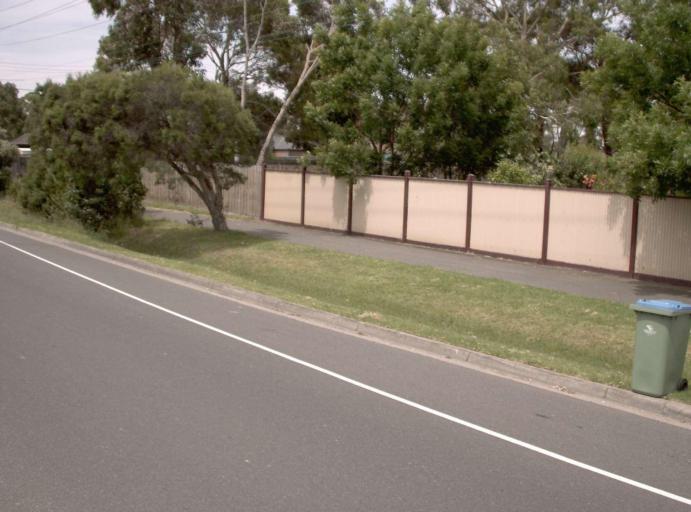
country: AU
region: Victoria
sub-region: Mornington Peninsula
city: Hastings
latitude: -38.2891
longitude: 145.1902
